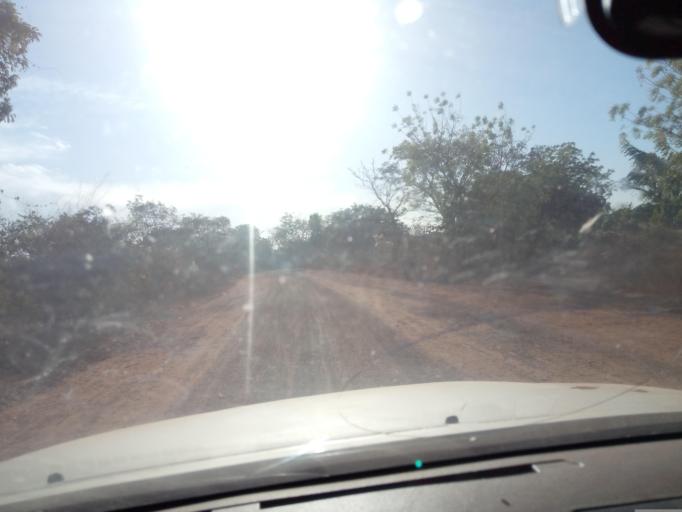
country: ML
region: Sikasso
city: Sikasso
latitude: 11.4824
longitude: -5.4903
